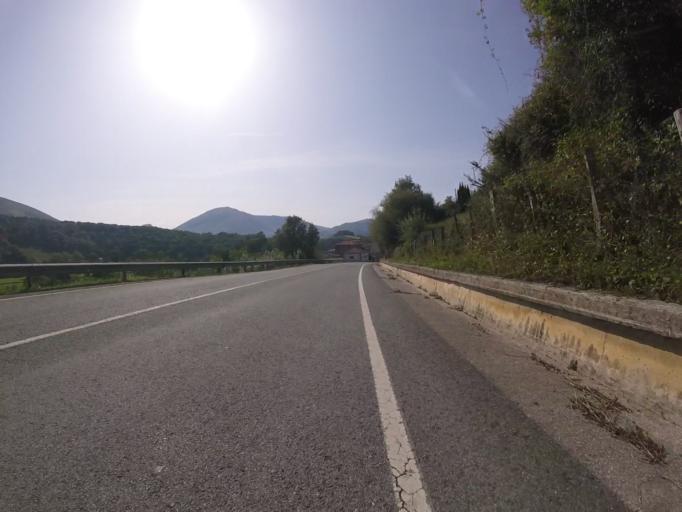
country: ES
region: Navarre
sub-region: Provincia de Navarra
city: Zugarramurdi
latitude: 43.1985
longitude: -1.4842
